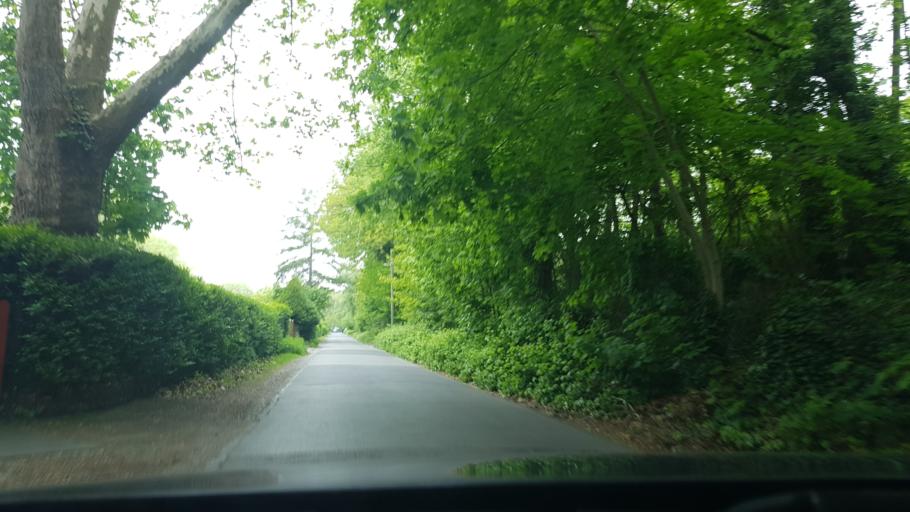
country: DE
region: North Rhine-Westphalia
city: Meiderich
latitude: 51.4999
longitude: 6.8152
